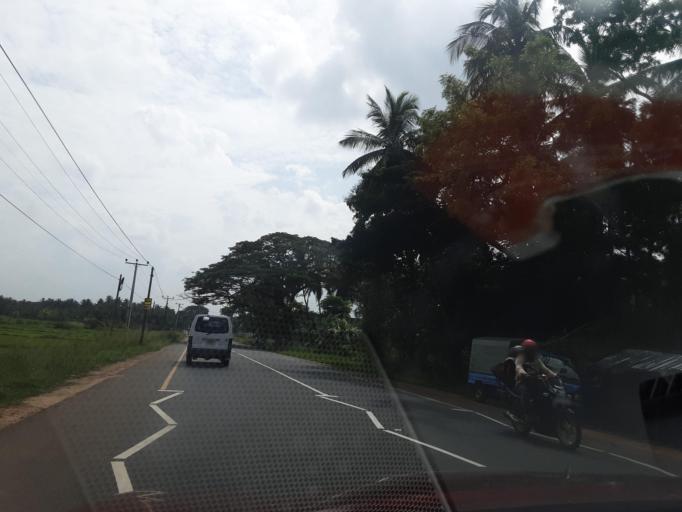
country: LK
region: North Central
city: Anuradhapura
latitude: 8.4765
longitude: 80.5128
